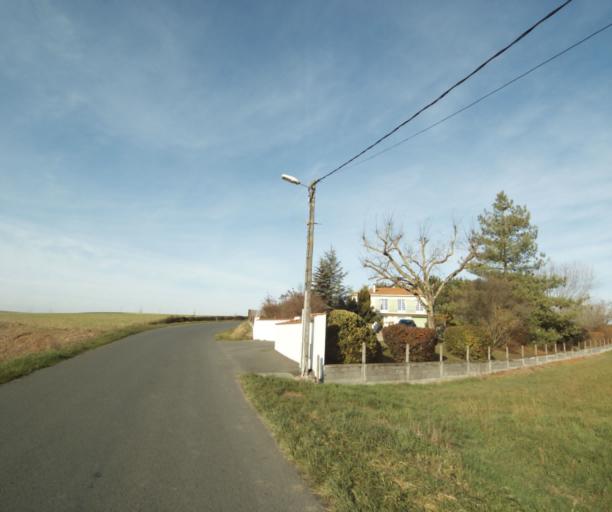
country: FR
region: Poitou-Charentes
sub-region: Departement de la Charente-Maritime
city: Chaniers
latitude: 45.7234
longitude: -0.5571
